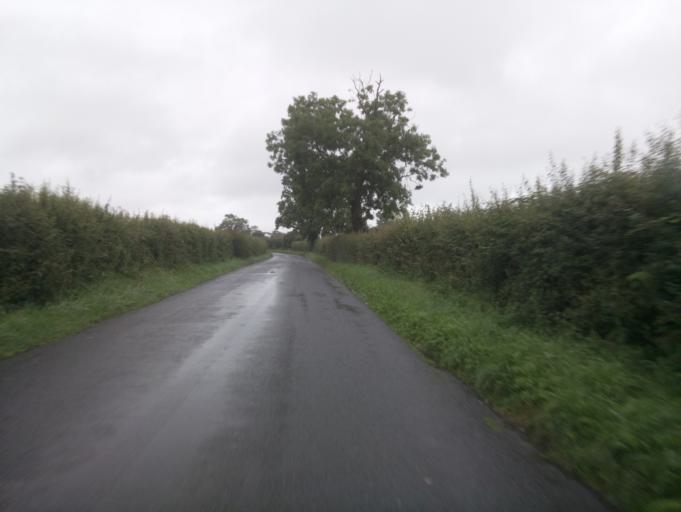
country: GB
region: England
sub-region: Gloucestershire
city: Uckington
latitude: 51.9273
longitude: -2.1179
